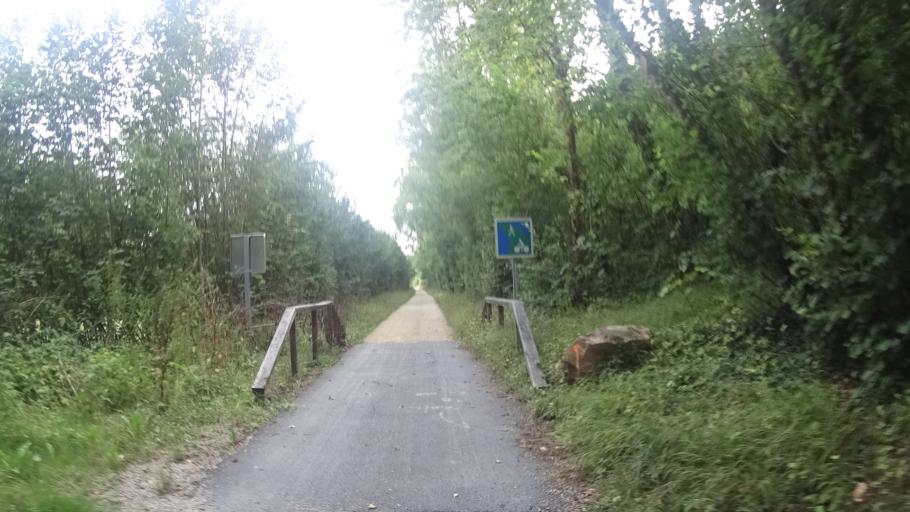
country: FR
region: Picardie
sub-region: Departement de l'Aisne
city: Origny-Sainte-Benoite
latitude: 49.8648
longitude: 3.5166
